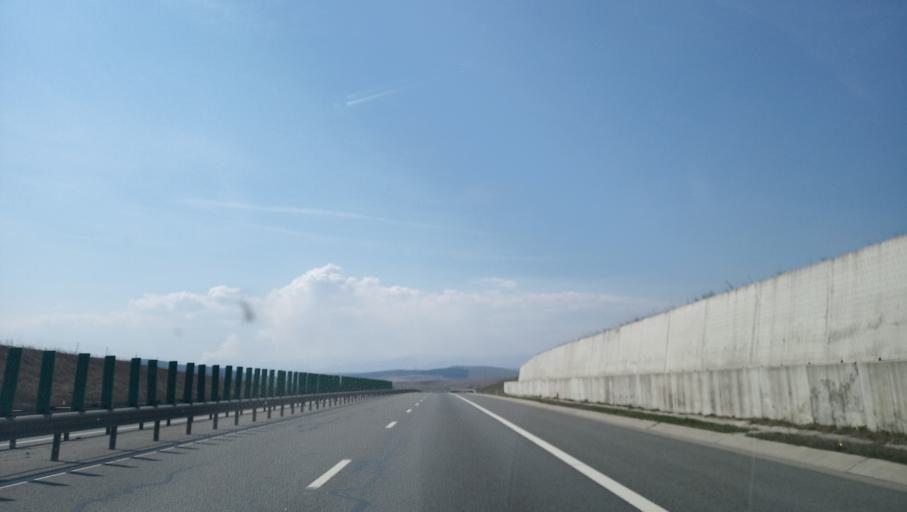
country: RO
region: Cluj
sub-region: Comuna Petrestii De Jos
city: Petrestii de Jos
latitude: 46.5993
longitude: 23.6645
